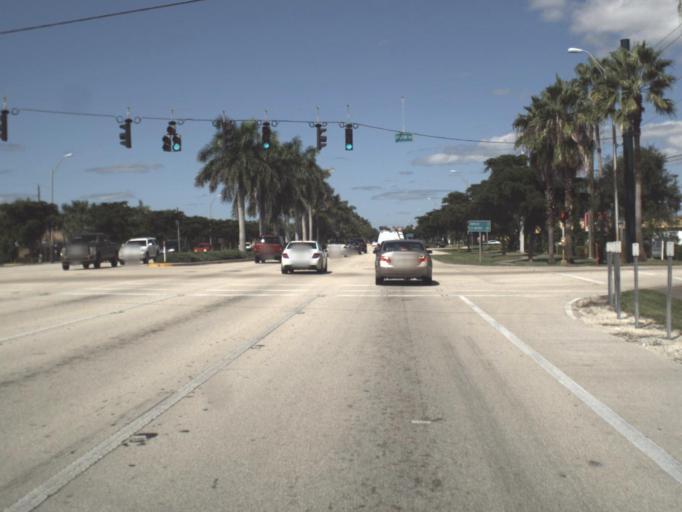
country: US
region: Florida
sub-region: Collier County
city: Lely
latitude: 26.1178
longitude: -81.7574
